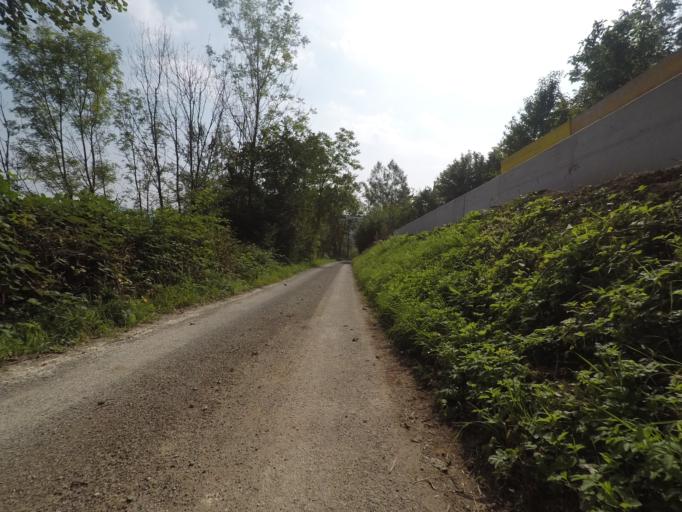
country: DE
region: Baden-Wuerttemberg
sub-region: Regierungsbezirk Stuttgart
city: Winterbach
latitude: 48.8041
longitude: 9.4259
